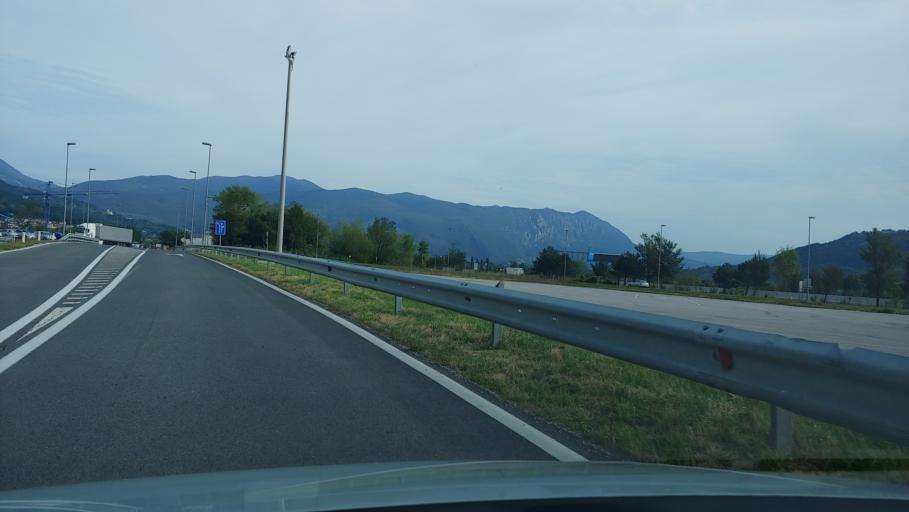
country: SI
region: Ajdovscina
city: Ajdovscina
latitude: 45.8833
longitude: 13.8929
